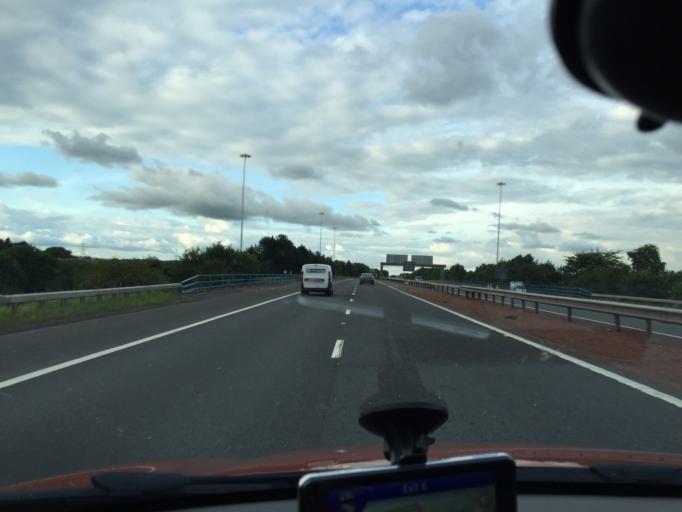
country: GB
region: Scotland
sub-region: South Lanarkshire
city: Uddingston
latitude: 55.8547
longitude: -4.0890
